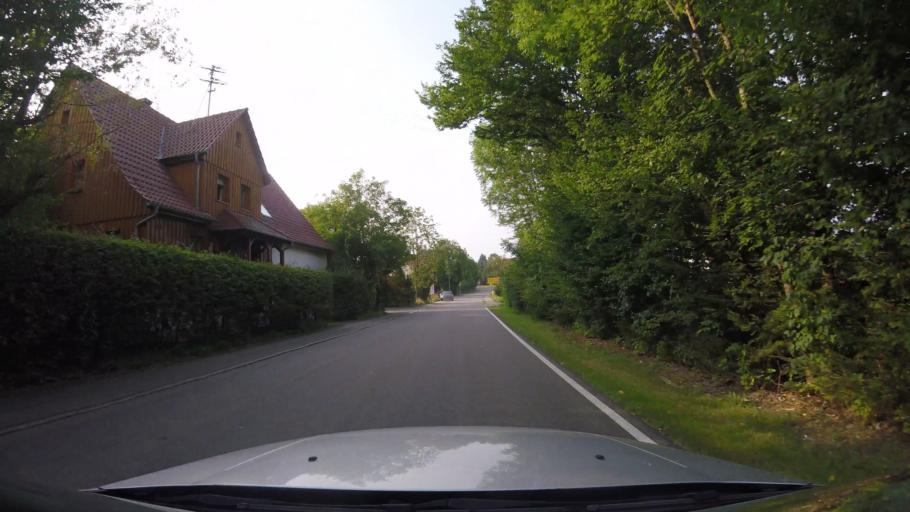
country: DE
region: Baden-Wuerttemberg
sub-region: Regierungsbezirk Stuttgart
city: Welzheim
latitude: 48.8551
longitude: 9.6264
